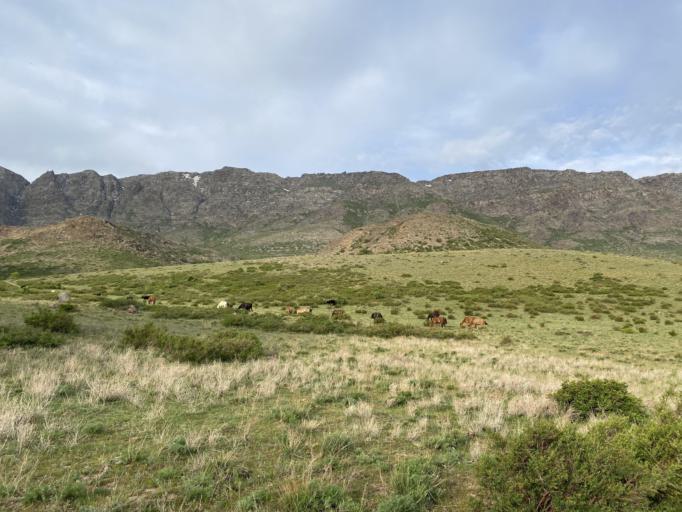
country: KZ
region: Ongtustik Qazaqstan
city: Kentau
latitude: 43.8674
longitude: 68.4992
